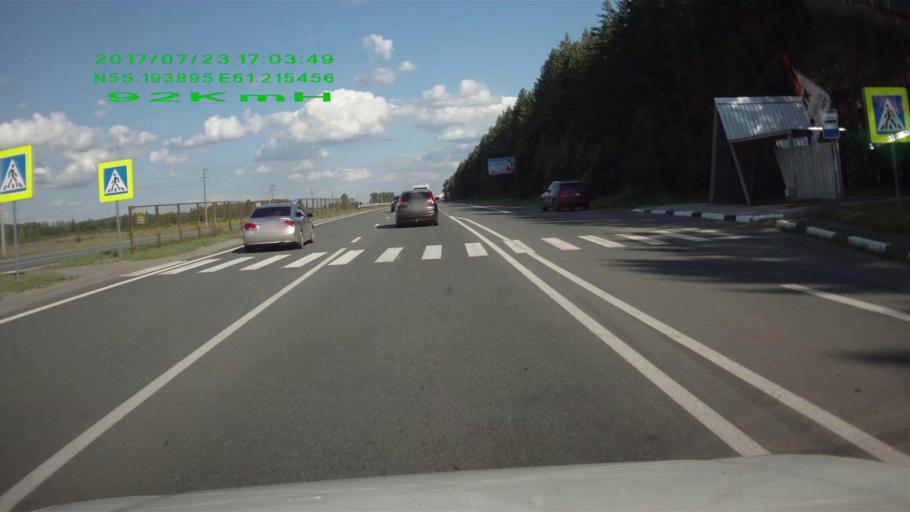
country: RU
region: Chelyabinsk
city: Roshchino
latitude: 55.1935
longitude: 61.2169
